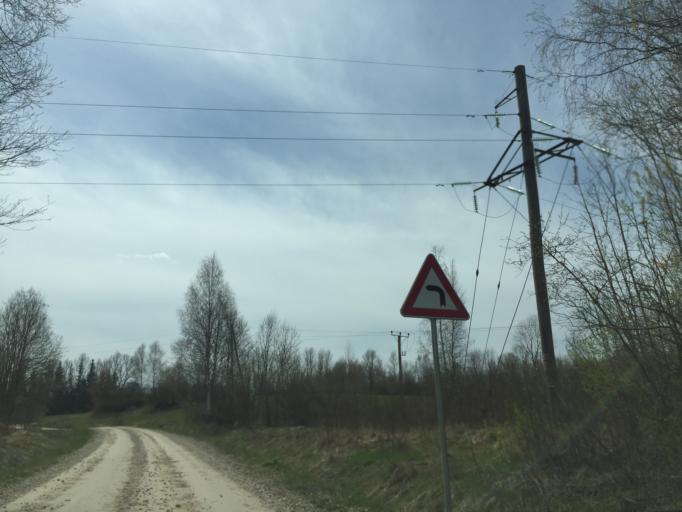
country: LV
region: Ludzas Rajons
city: Ludza
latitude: 56.5376
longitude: 27.5277
